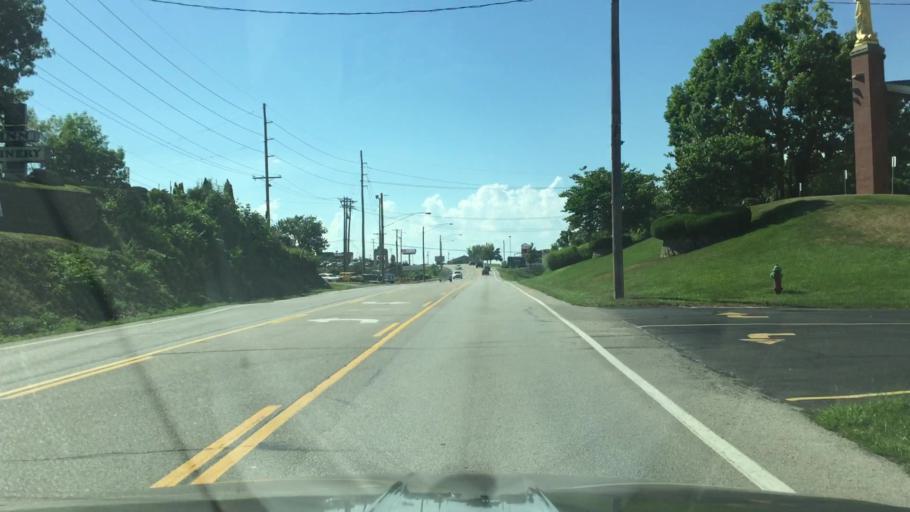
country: US
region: Missouri
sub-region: Miller County
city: Lake Ozark
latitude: 38.1851
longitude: -92.6375
